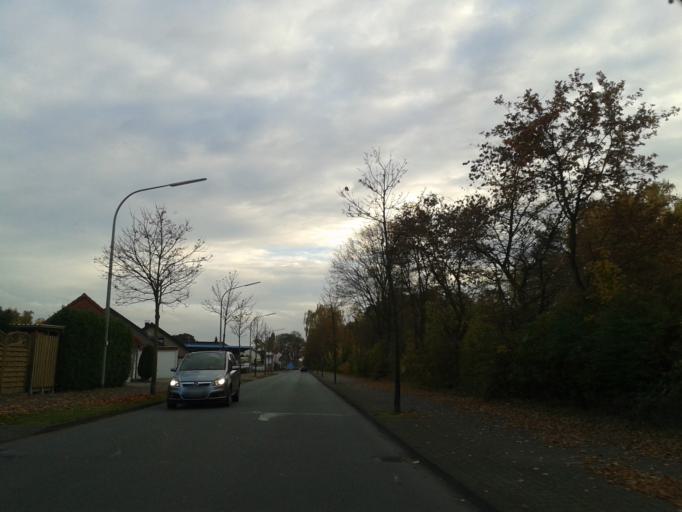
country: DE
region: North Rhine-Westphalia
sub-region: Regierungsbezirk Detmold
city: Paderborn
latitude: 51.7613
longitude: 8.7193
